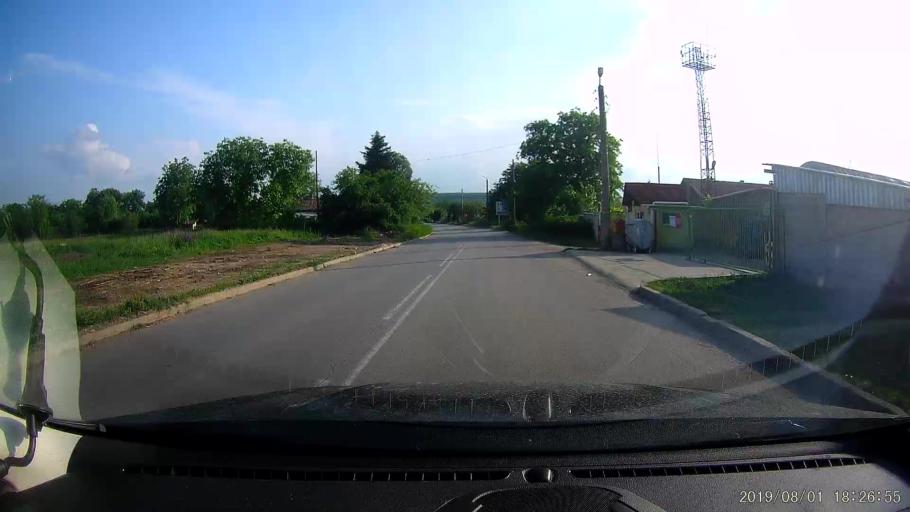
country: BG
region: Shumen
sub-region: Obshtina Venets
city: Venets
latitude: 43.5941
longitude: 26.9838
